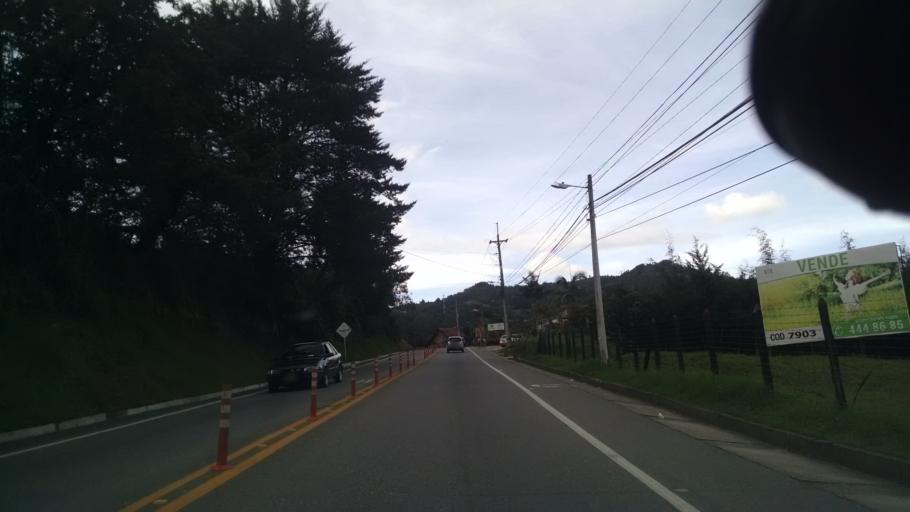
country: CO
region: Antioquia
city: El Retiro
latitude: 6.1181
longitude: -75.5007
